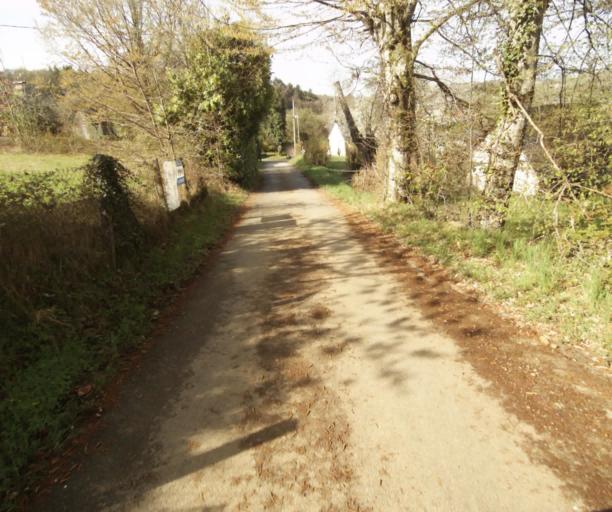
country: FR
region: Limousin
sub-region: Departement de la Correze
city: Laguenne
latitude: 45.2639
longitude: 1.8228
